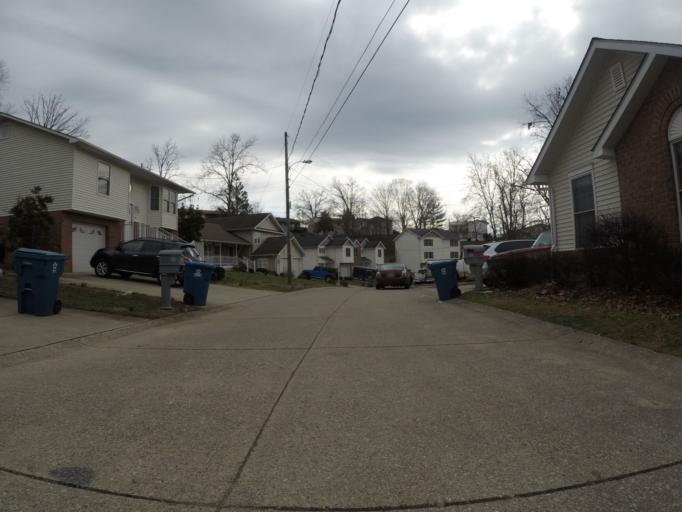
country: US
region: West Virginia
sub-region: Cabell County
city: Pea Ridge
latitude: 38.3935
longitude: -82.3794
